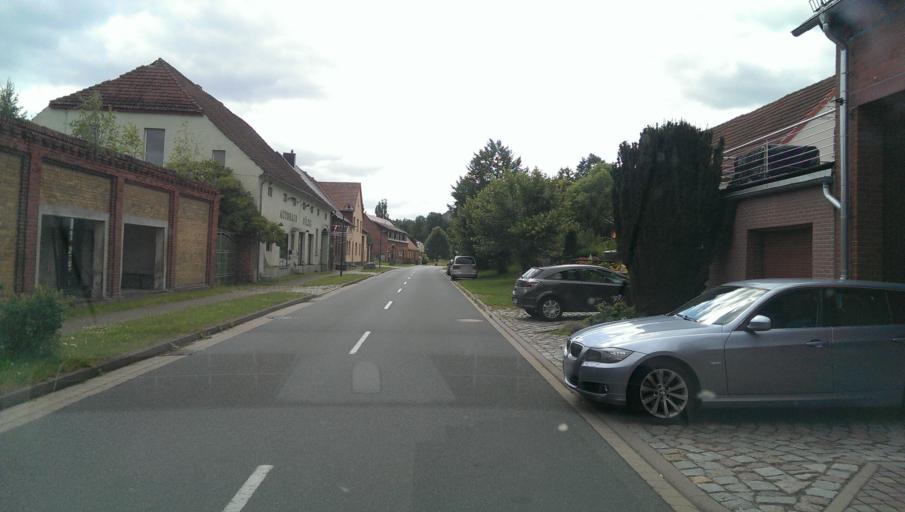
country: DE
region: Saxony-Anhalt
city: Nudersdorf
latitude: 51.9432
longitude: 12.5511
